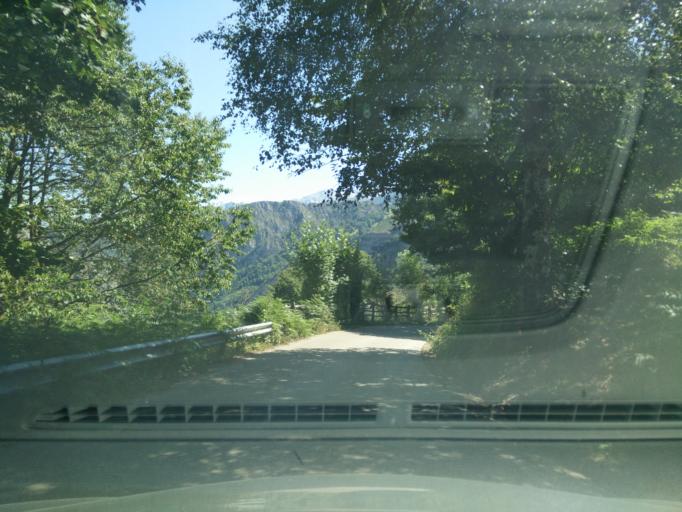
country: ES
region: Asturias
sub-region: Province of Asturias
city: Amieva
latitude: 43.1952
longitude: -5.1280
